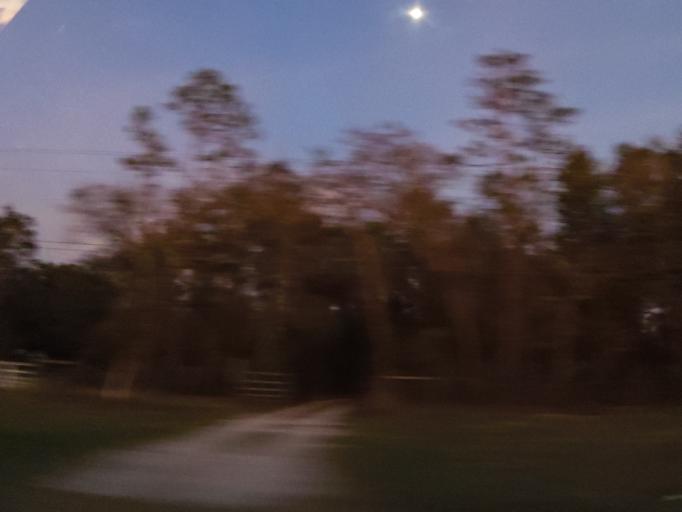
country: US
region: Florida
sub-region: Volusia County
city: De Leon Springs
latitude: 29.2107
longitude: -81.3147
